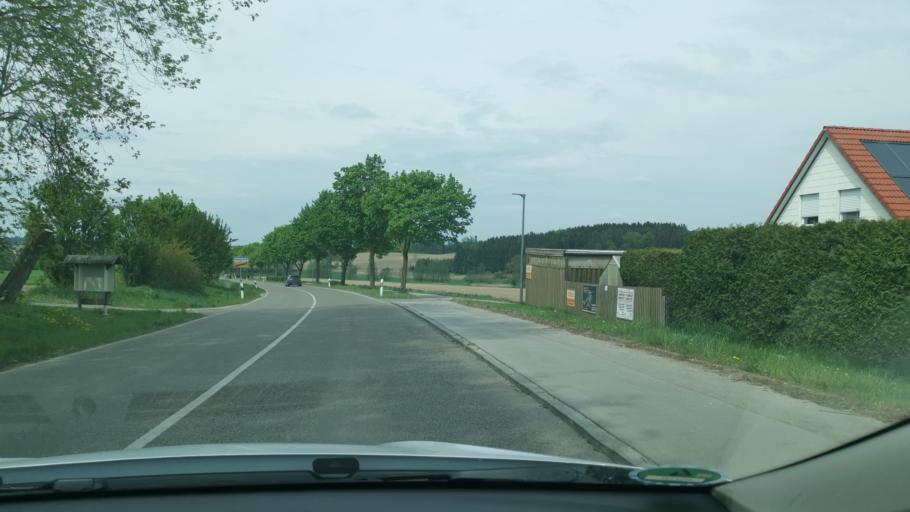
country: DE
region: Bavaria
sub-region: Upper Bavaria
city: Petershausen
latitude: 48.3940
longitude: 11.4833
